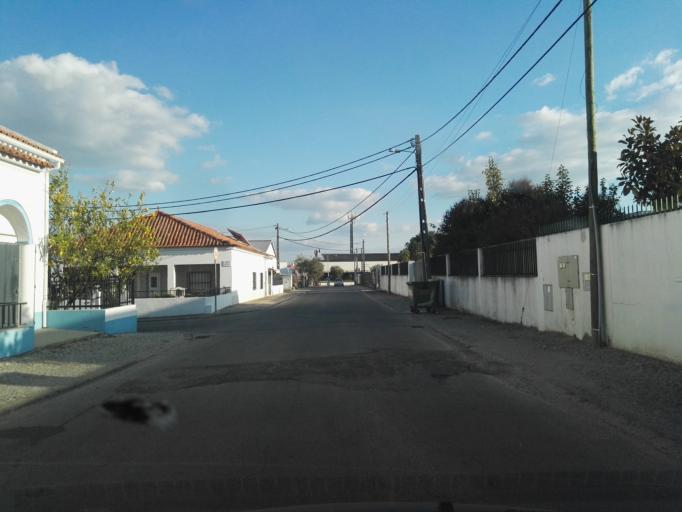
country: PT
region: Evora
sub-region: Evora
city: Evora
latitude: 38.5611
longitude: -7.9238
